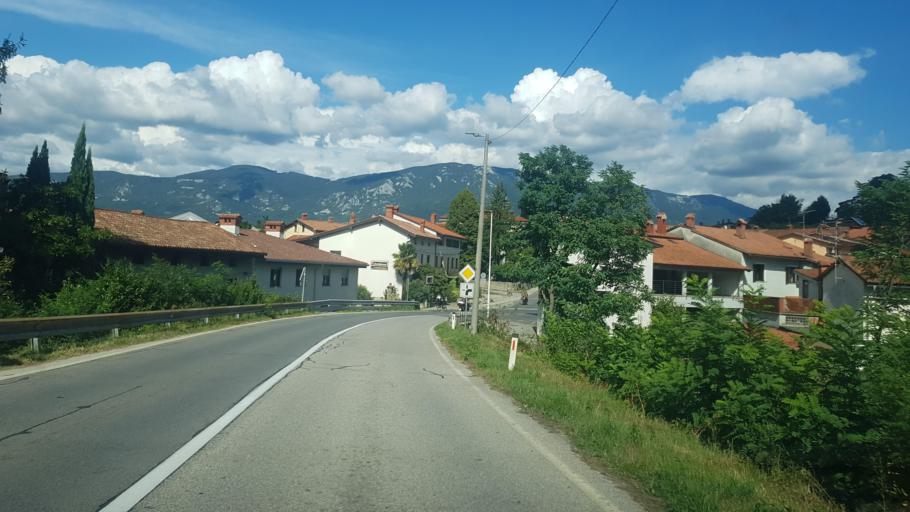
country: SI
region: Nova Gorica
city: Prvacina
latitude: 45.8857
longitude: 13.7346
